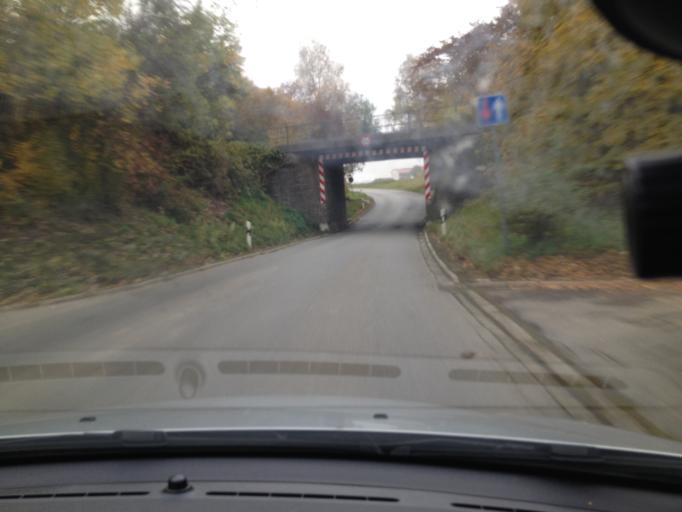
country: DE
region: Bavaria
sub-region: Swabia
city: Schwabmunchen
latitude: 48.1871
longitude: 10.7739
